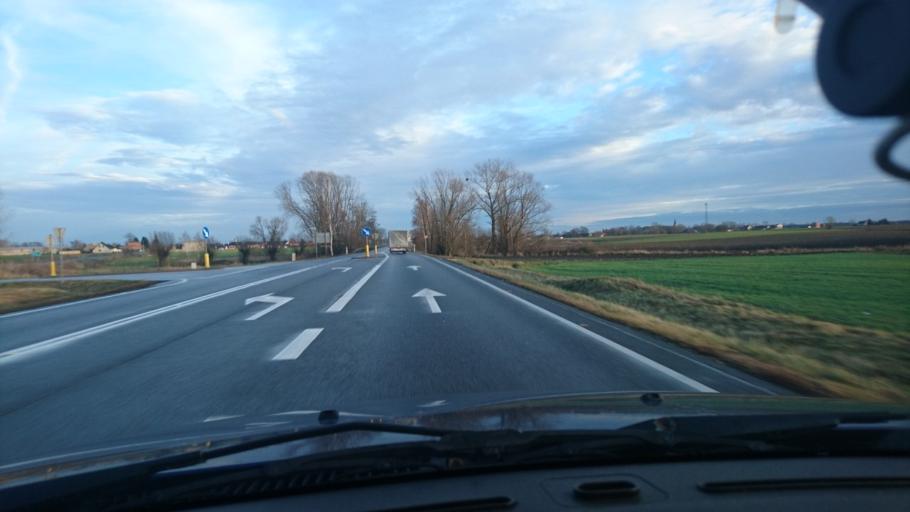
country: PL
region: Greater Poland Voivodeship
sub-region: Powiat kepinski
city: Opatow
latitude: 51.2215
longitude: 18.1289
